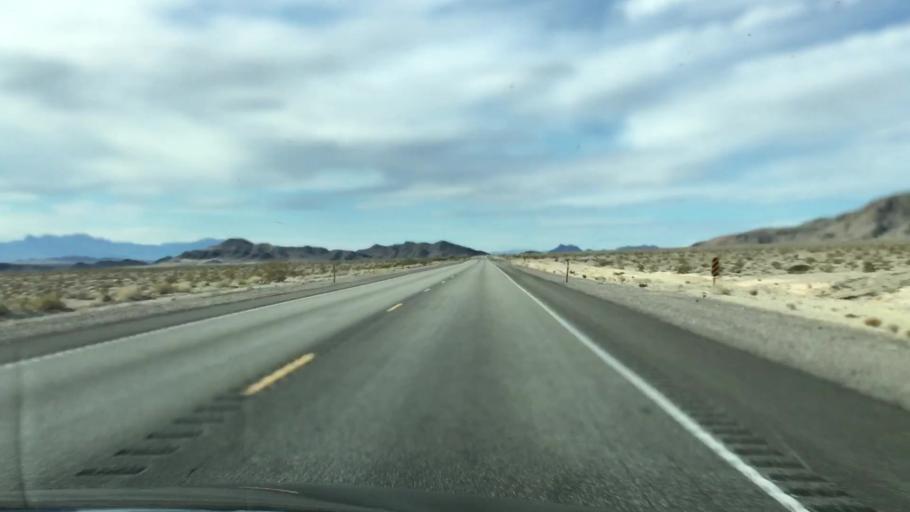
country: US
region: Nevada
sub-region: Nye County
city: Pahrump
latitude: 36.5711
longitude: -116.1673
